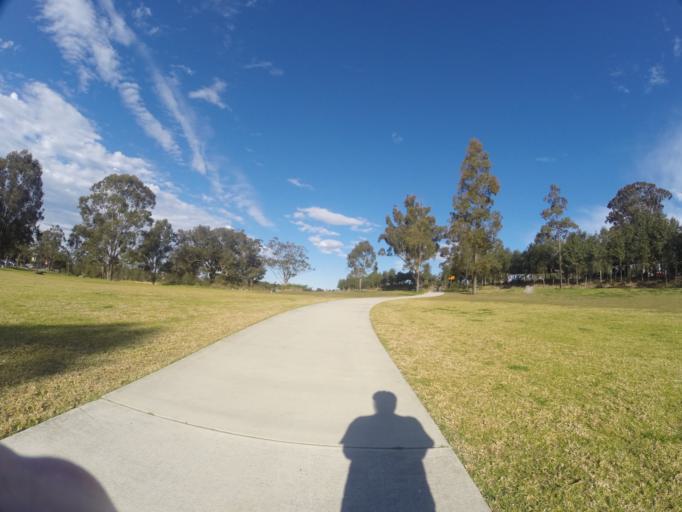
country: AU
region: New South Wales
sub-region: Fairfield
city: Horsley Park
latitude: -33.8506
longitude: 150.8716
